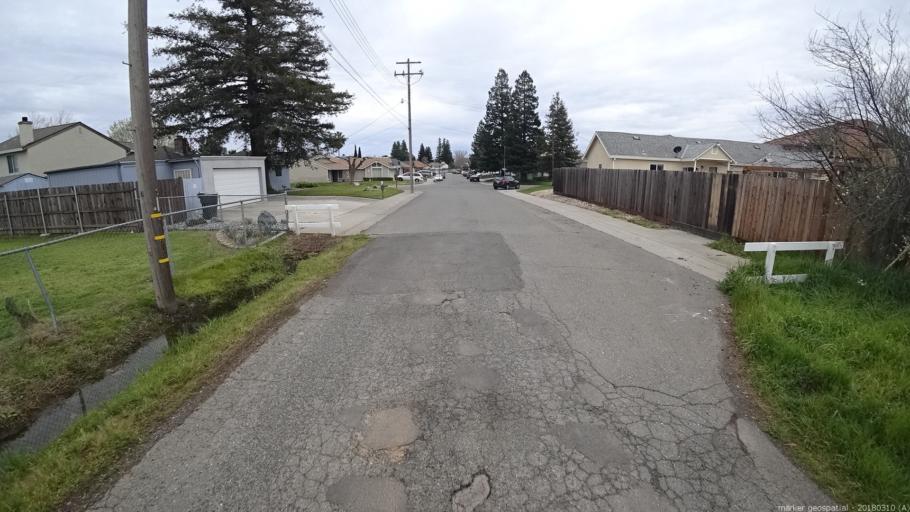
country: US
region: California
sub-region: Sacramento County
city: Vineyard
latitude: 38.4672
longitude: -121.3811
